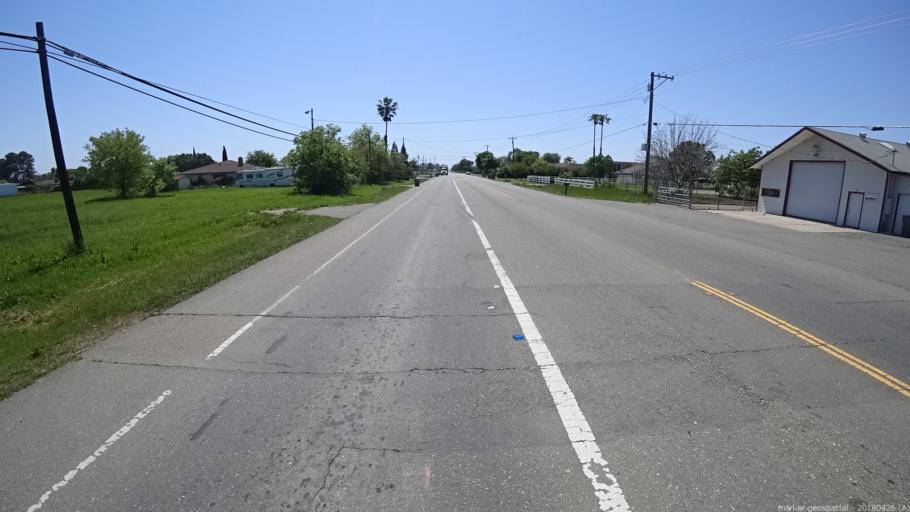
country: US
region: California
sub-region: Yolo County
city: West Sacramento
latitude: 38.5347
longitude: -121.5541
